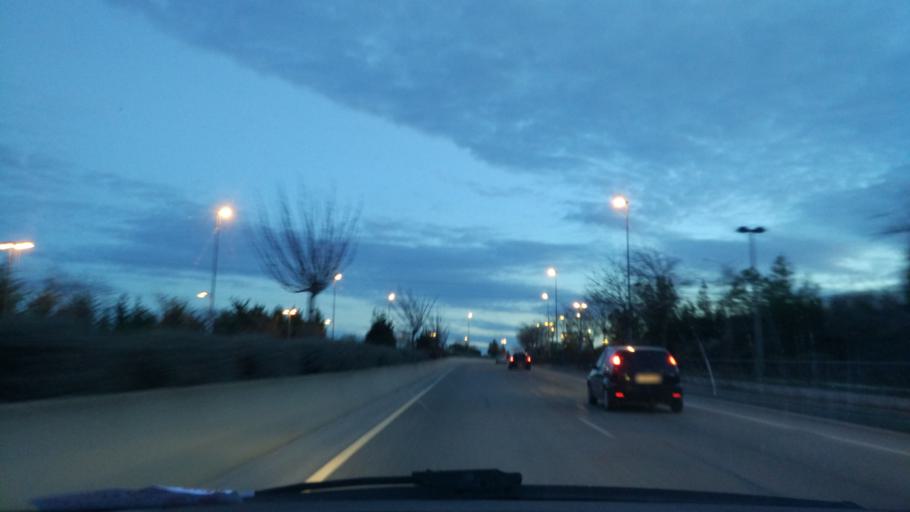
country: ES
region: Madrid
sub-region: Provincia de Madrid
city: Leganes
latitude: 40.3530
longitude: -3.7718
